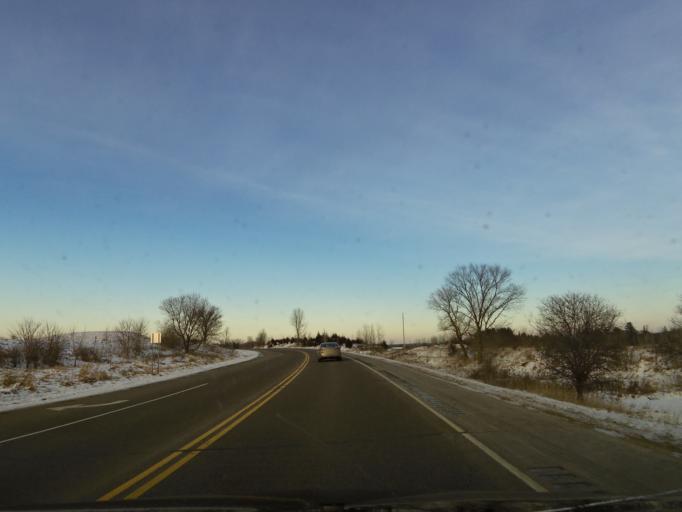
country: US
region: Wisconsin
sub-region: Polk County
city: Osceola
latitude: 45.3494
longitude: -92.7134
